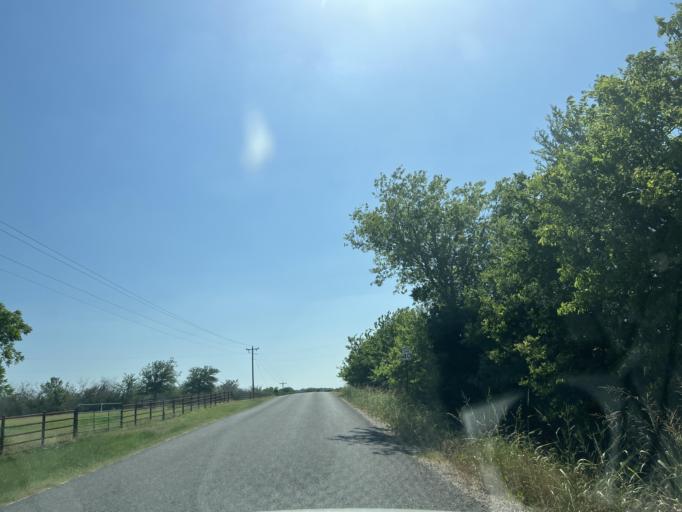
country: US
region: Texas
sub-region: Washington County
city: Brenham
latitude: 30.1583
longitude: -96.3445
